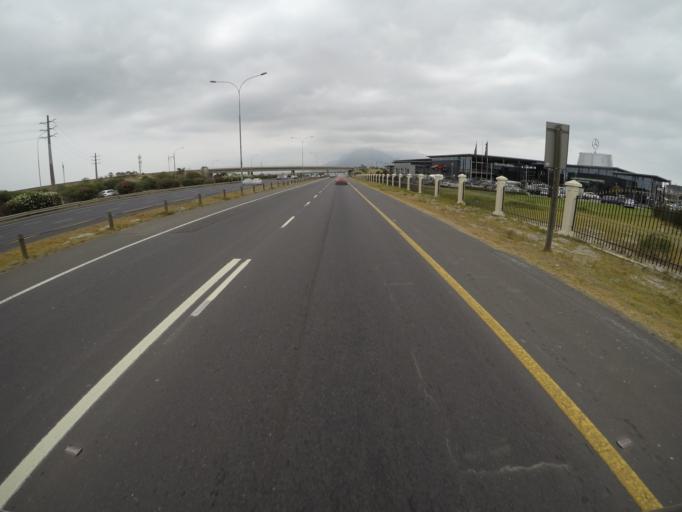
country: ZA
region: Western Cape
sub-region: City of Cape Town
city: Sunset Beach
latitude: -33.8966
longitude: 18.5139
